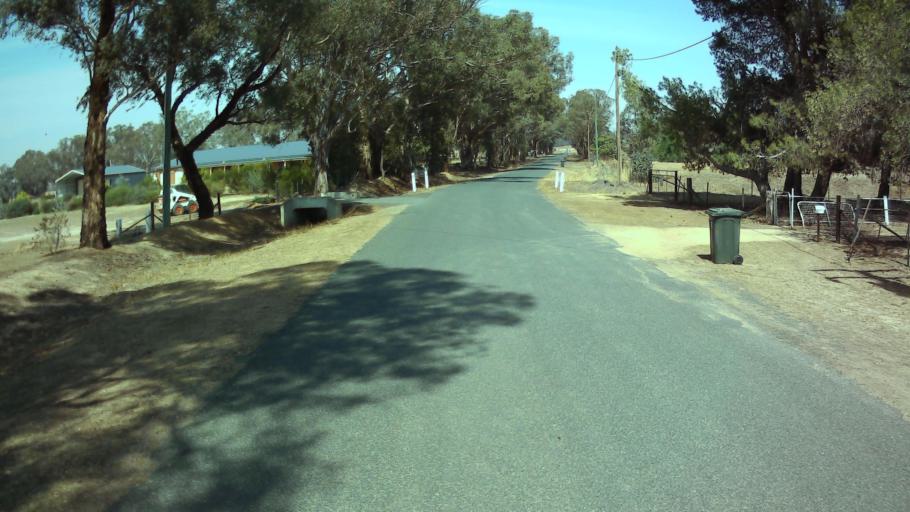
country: AU
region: New South Wales
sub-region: Weddin
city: Grenfell
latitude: -33.8956
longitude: 148.1456
